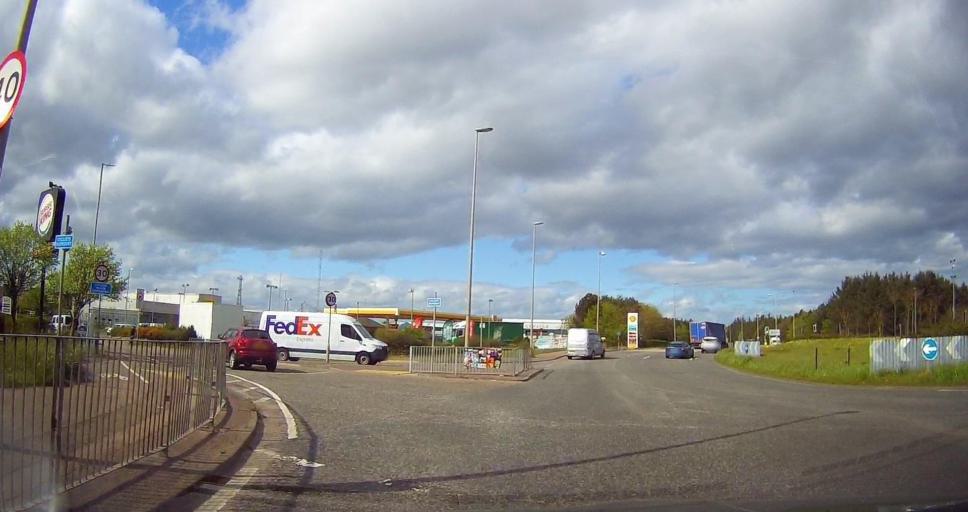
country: GB
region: Scotland
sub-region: Aberdeen City
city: Aberdeen
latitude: 57.1087
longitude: -2.0927
